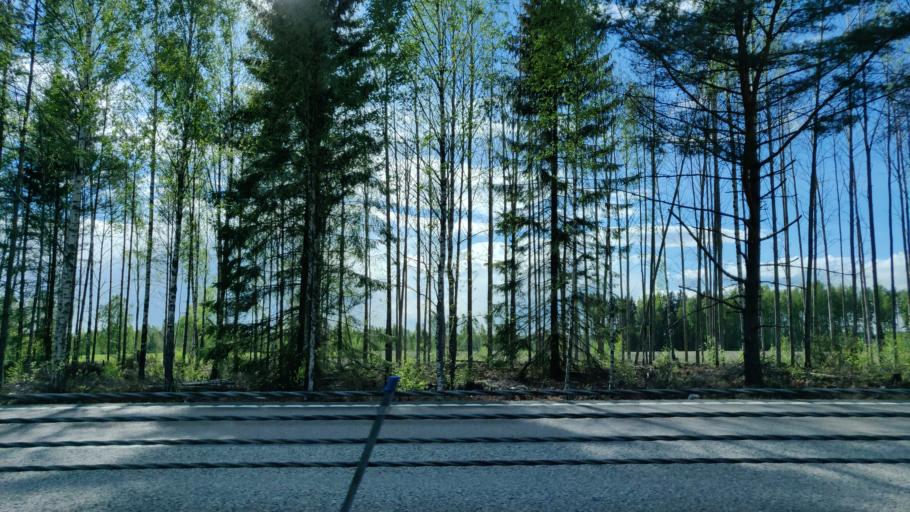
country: SE
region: Vaermland
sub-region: Forshaga Kommun
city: Forshaga
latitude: 59.4734
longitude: 13.4110
